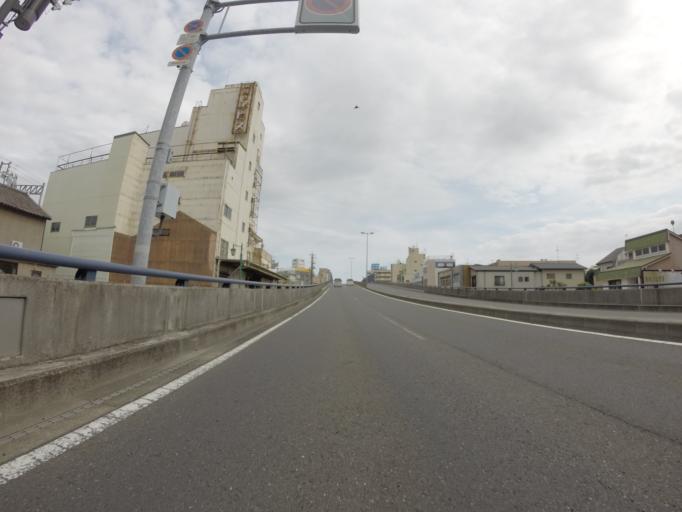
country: JP
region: Shizuoka
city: Shizuoka-shi
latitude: 35.0202
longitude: 138.4874
